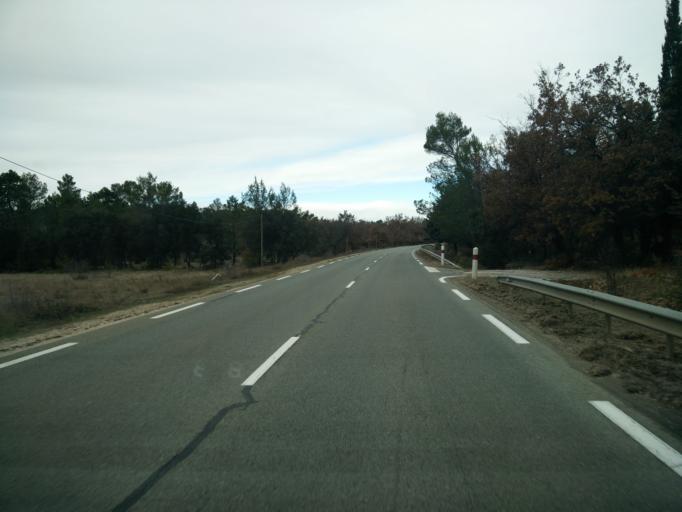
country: FR
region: Provence-Alpes-Cote d'Azur
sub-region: Departement du Var
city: Camps-la-Source
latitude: 43.3680
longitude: 6.0912
